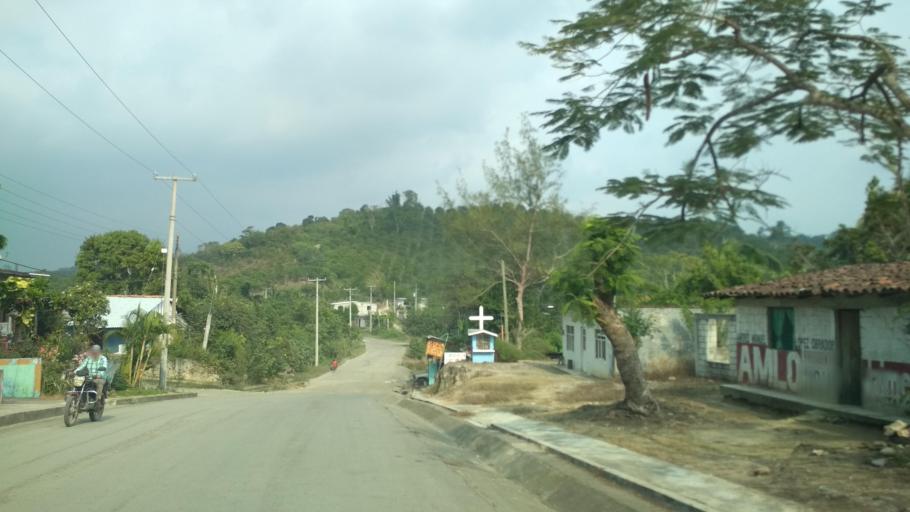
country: MM
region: Kayah
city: Loikaw
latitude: 20.2396
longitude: 97.2761
